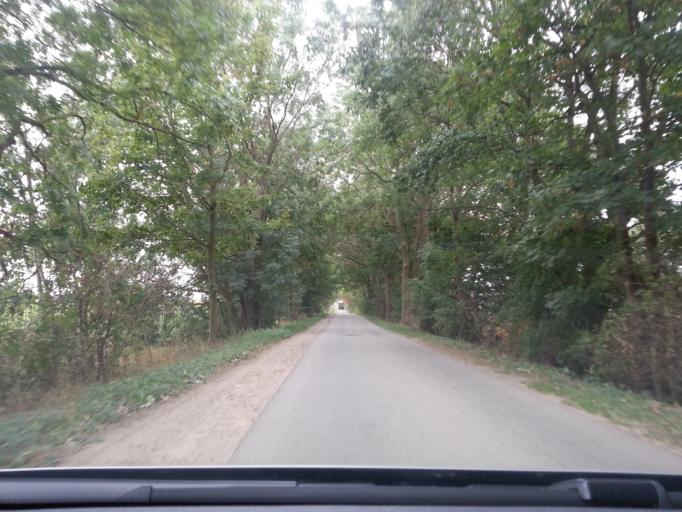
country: DE
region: Mecklenburg-Vorpommern
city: Ferdinandshof
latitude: 53.6708
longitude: 13.9161
